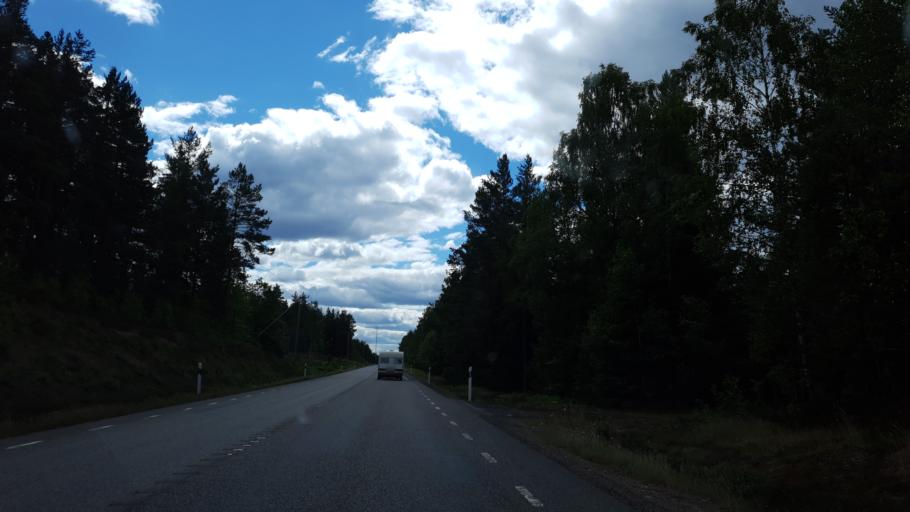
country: SE
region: Kronoberg
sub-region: Vaxjo Kommun
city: Braas
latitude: 57.1460
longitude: 15.1632
